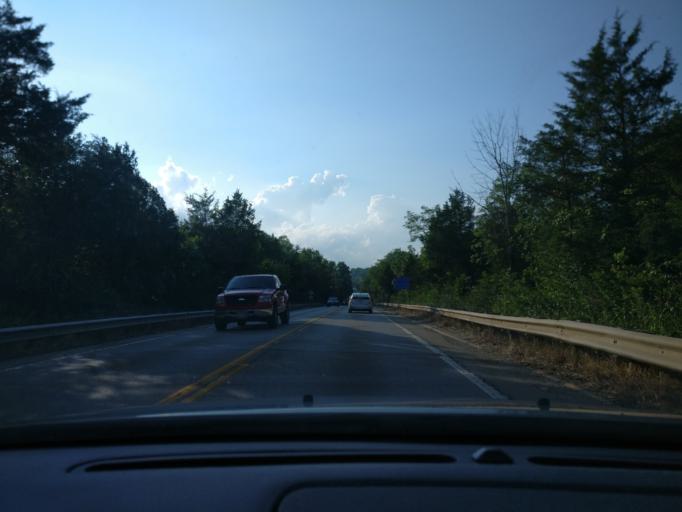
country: US
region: Ohio
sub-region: Warren County
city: Waynesville
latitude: 39.5227
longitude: -84.0851
